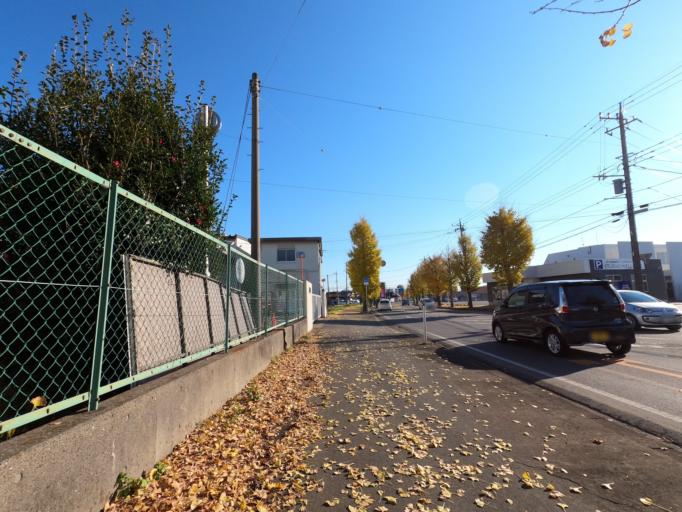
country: JP
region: Ibaraki
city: Moriya
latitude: 35.9549
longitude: 139.9792
